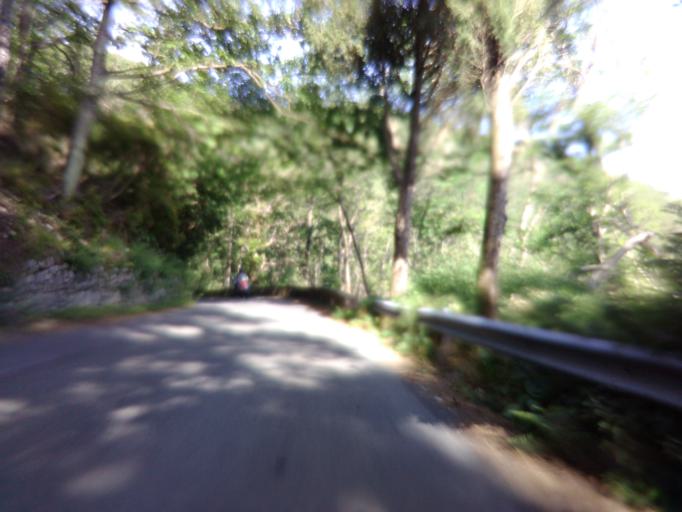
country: IT
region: Tuscany
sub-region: Provincia di Massa-Carrara
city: Fosdinovo
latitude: 44.1204
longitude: 10.0621
